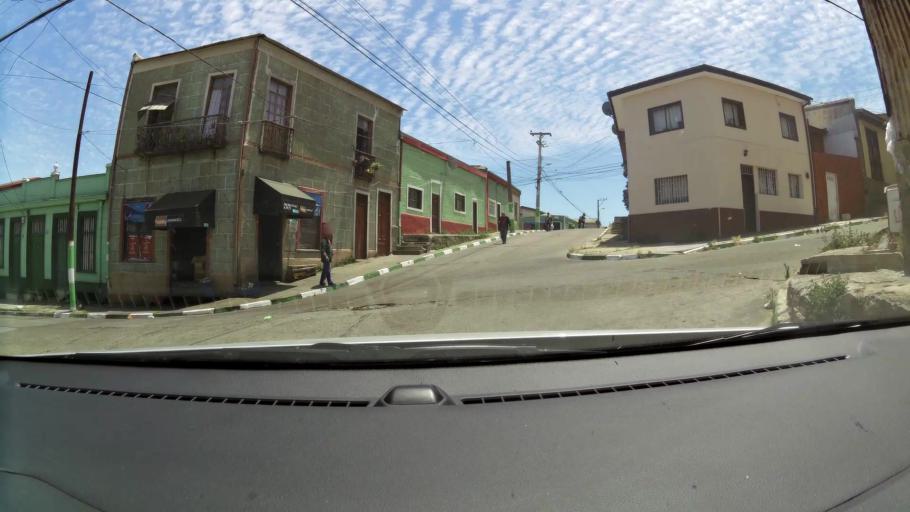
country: CL
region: Valparaiso
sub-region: Provincia de Valparaiso
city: Valparaiso
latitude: -33.0434
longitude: -71.5990
